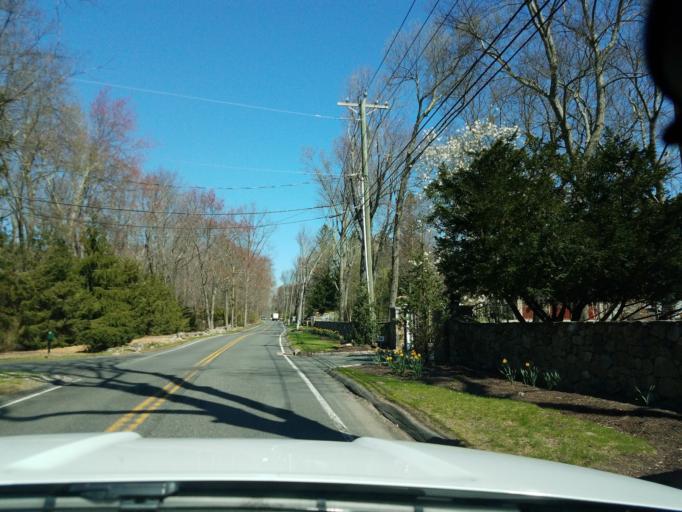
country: US
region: Connecticut
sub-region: Fairfield County
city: Wilton
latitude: 41.2139
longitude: -73.3755
